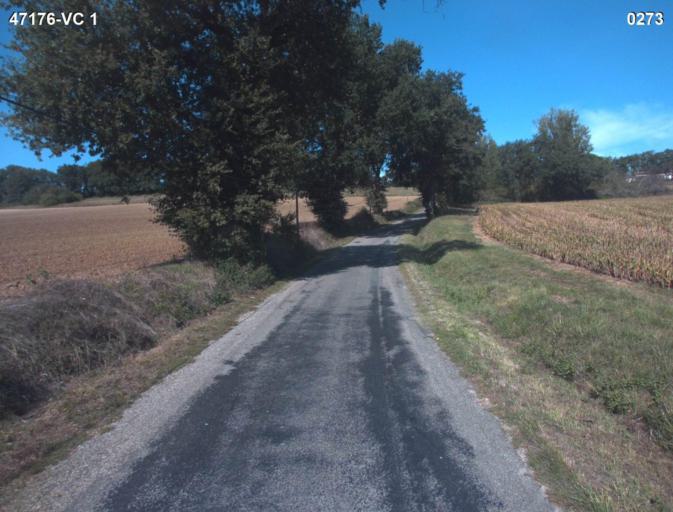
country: FR
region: Aquitaine
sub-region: Departement du Lot-et-Garonne
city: Lavardac
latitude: 44.1954
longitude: 0.2924
